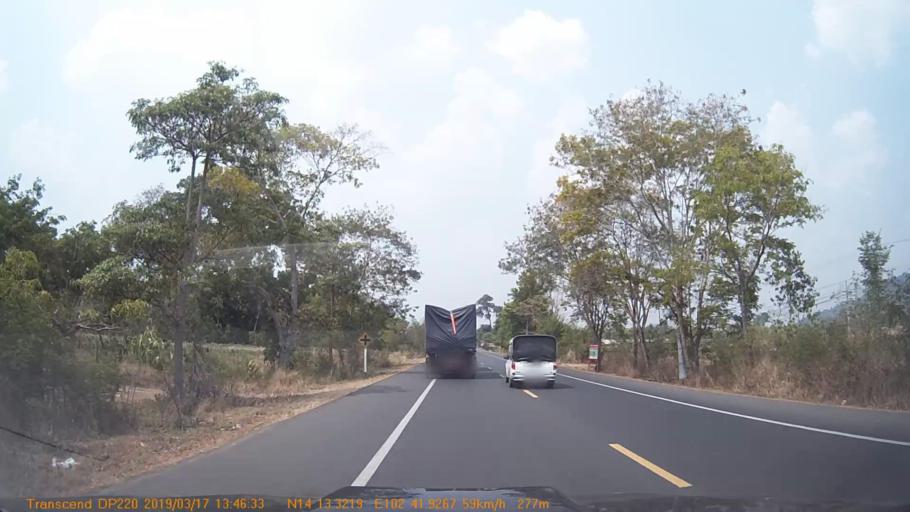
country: TH
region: Buriram
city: Non Din Daeng
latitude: 14.2223
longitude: 102.6987
